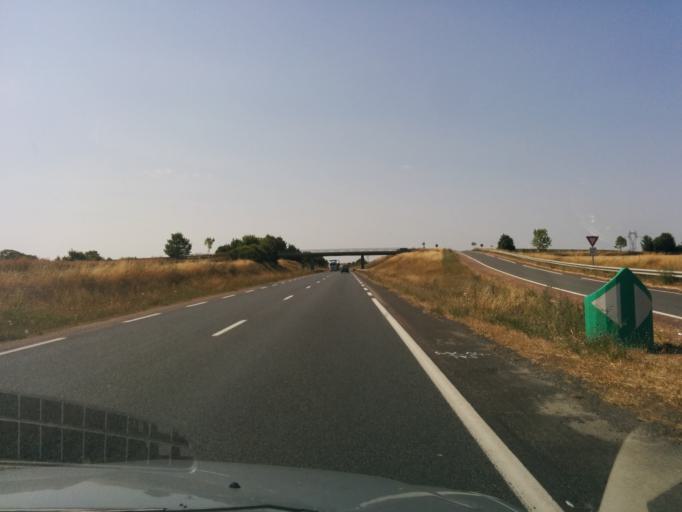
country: FR
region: Poitou-Charentes
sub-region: Departement de la Vienne
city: Neuville-de-Poitou
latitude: 46.7090
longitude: 0.2303
